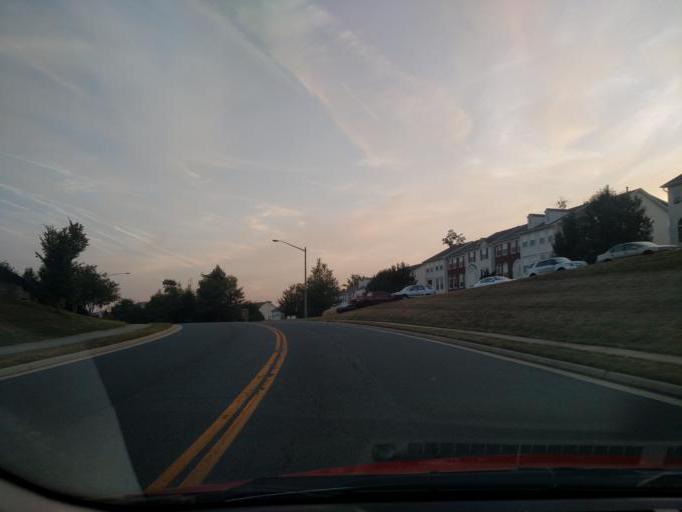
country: US
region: Virginia
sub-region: Prince William County
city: Woodbridge
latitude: 38.6151
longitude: -77.2574
